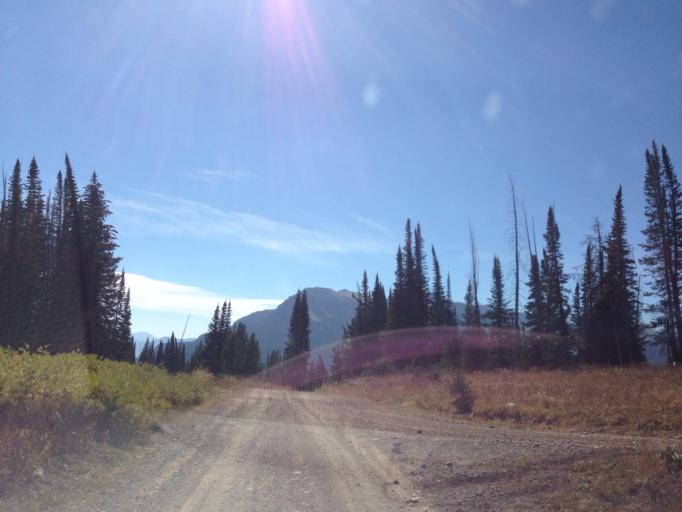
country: US
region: Montana
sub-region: Stillwater County
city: Absarokee
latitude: 45.0444
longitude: -109.9126
